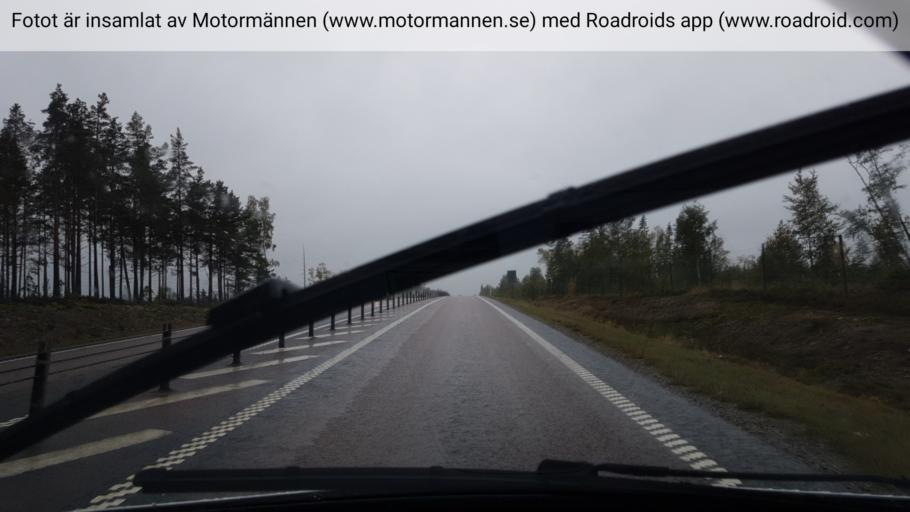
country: SE
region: Gaevleborg
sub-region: Hudiksvalls Kommun
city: Hudiksvall
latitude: 61.8200
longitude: 17.1906
